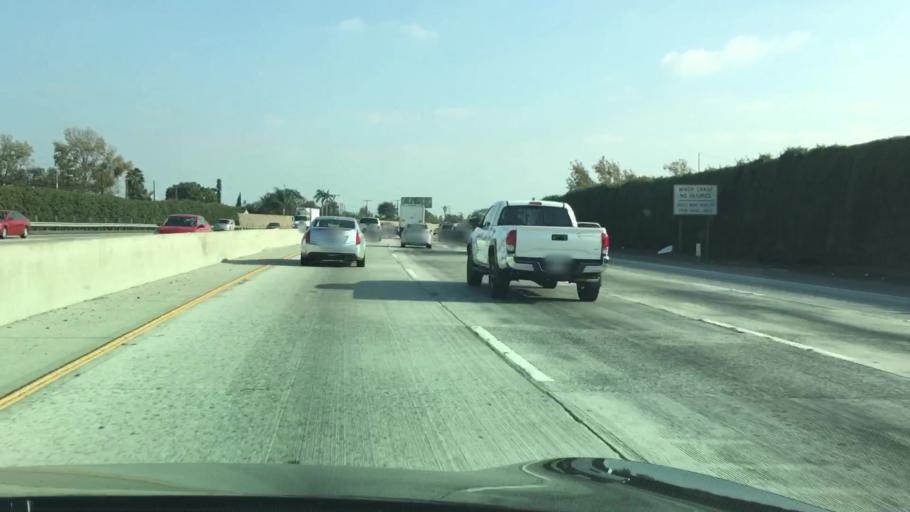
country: US
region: California
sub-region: Los Angeles County
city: Santa Fe Springs
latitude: 33.9530
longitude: -118.1051
